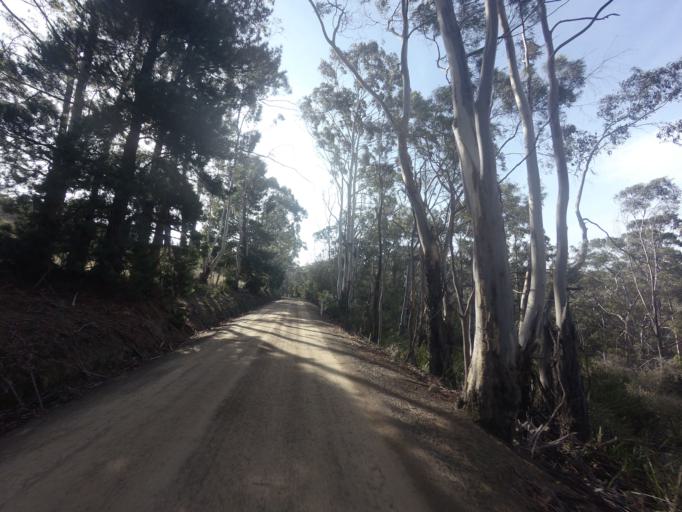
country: AU
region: Tasmania
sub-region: Kingborough
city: Kettering
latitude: -43.1050
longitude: 147.2600
